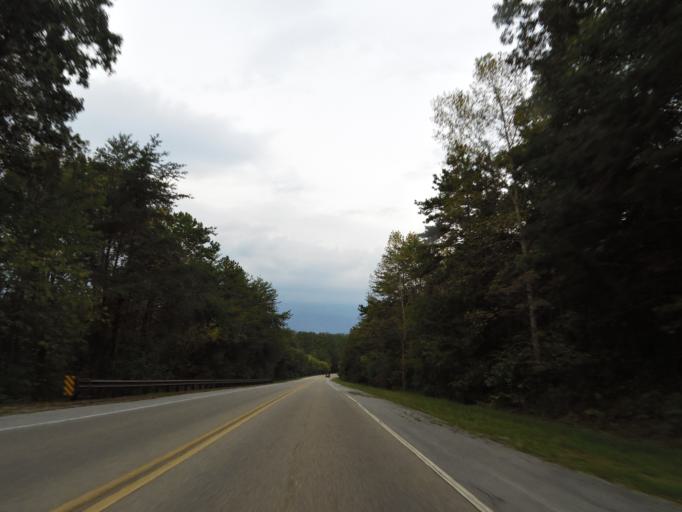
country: US
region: Tennessee
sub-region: Loudon County
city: Loudon
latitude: 35.6870
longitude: -84.2631
